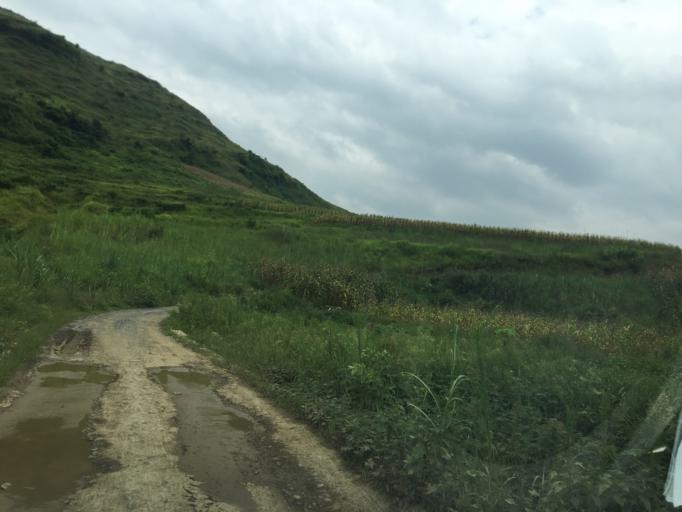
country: CN
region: Guangxi Zhuangzu Zizhiqu
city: Xinzhou
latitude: 25.1809
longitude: 105.7307
